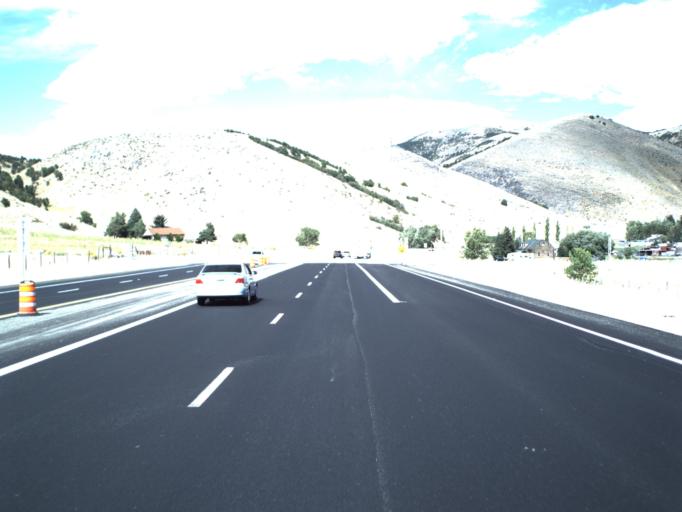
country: US
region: Utah
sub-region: Box Elder County
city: Brigham City
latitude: 41.5060
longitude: -111.9455
